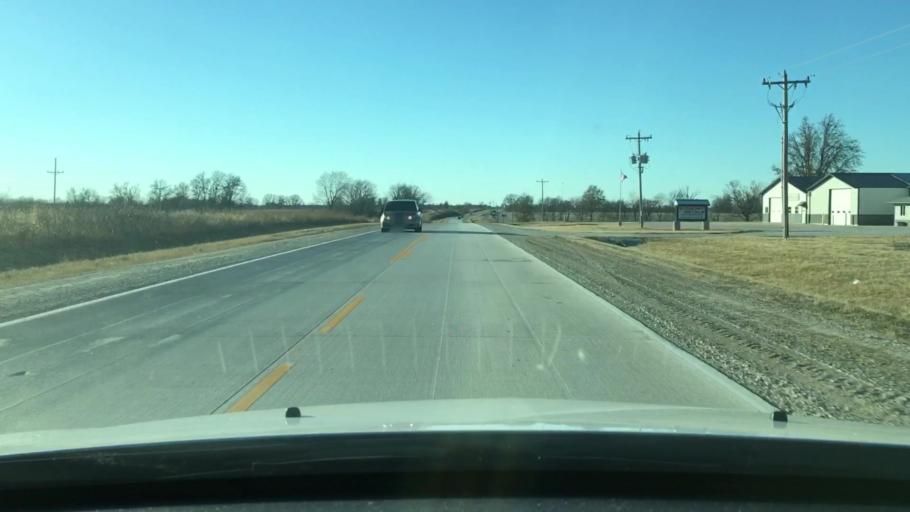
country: US
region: Missouri
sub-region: Boone County
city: Centralia
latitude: 39.2012
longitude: -92.0626
